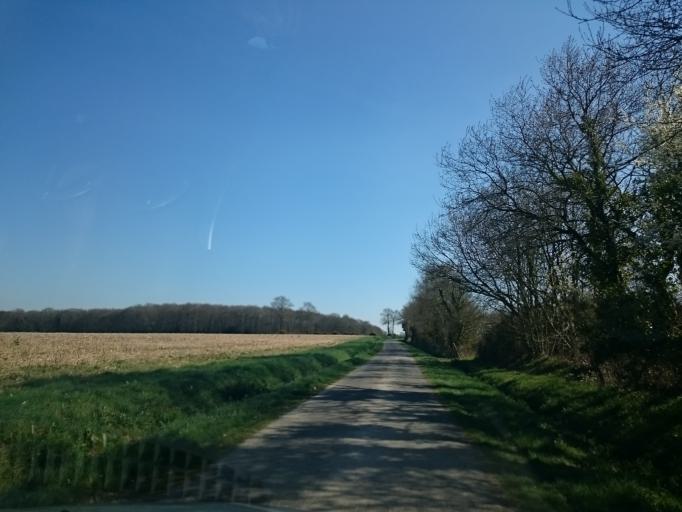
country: FR
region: Brittany
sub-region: Departement d'Ille-et-Vilaine
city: Chanteloup
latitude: 47.9542
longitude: -1.6430
